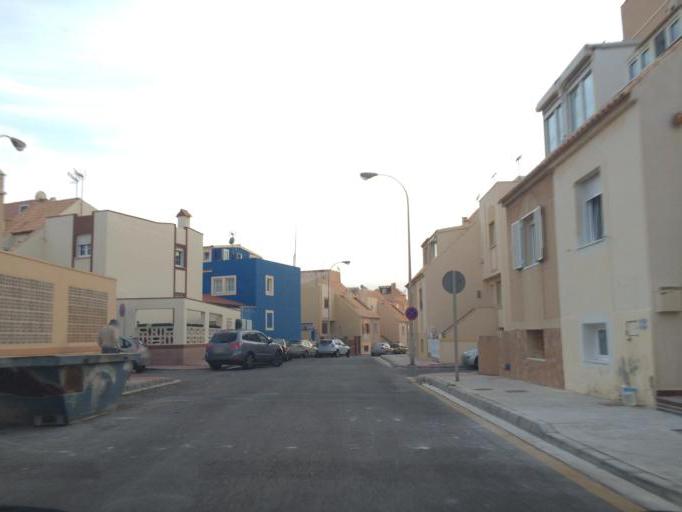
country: ES
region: Andalusia
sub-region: Provincia de Almeria
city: Almeria
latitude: 36.8218
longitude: -2.4406
